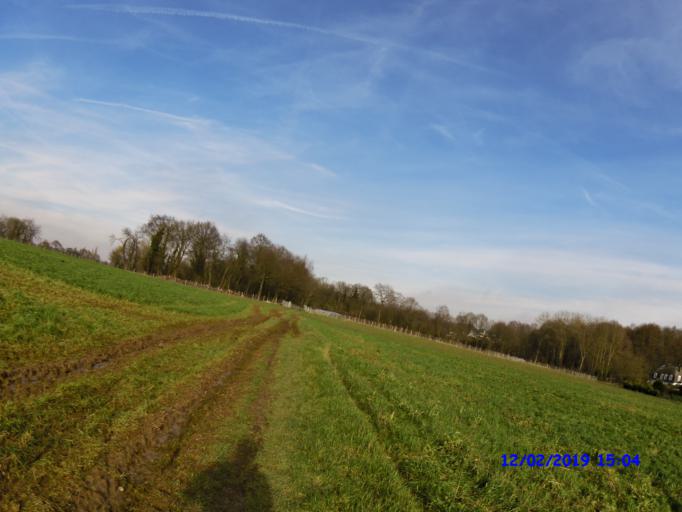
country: BE
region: Flanders
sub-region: Provincie Vlaams-Brabant
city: Sint-Genesius-Rode
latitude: 50.7588
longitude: 4.3631
